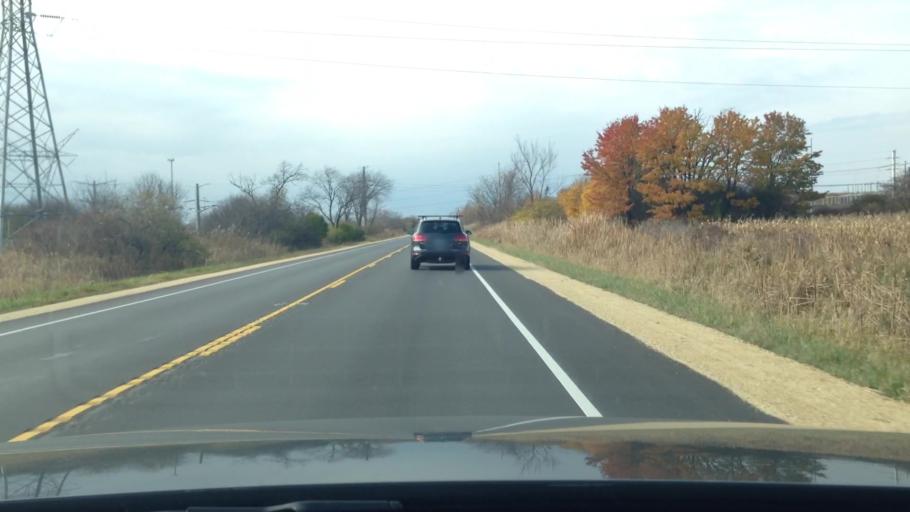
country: US
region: Illinois
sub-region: McHenry County
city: Woodstock
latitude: 42.2551
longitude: -88.4368
